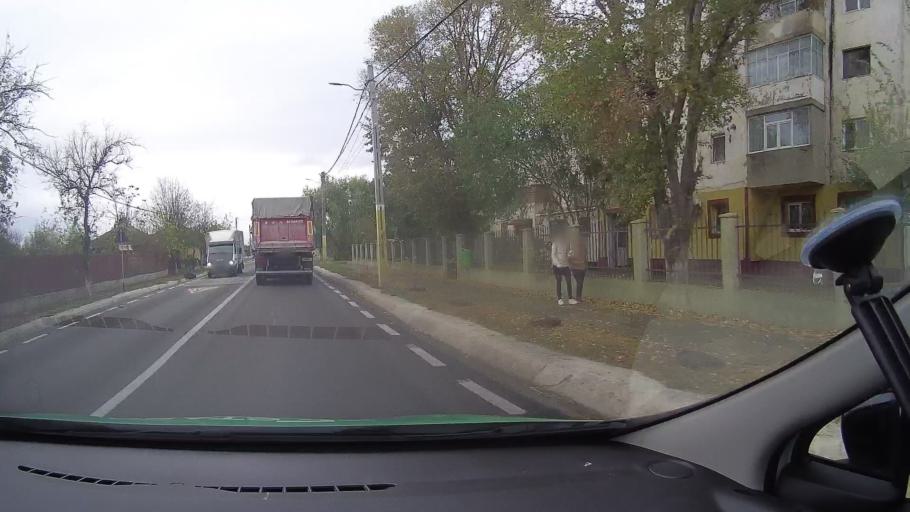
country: RO
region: Constanta
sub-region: Comuna Poarta Alba
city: Poarta Alba
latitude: 44.2076
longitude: 28.3948
